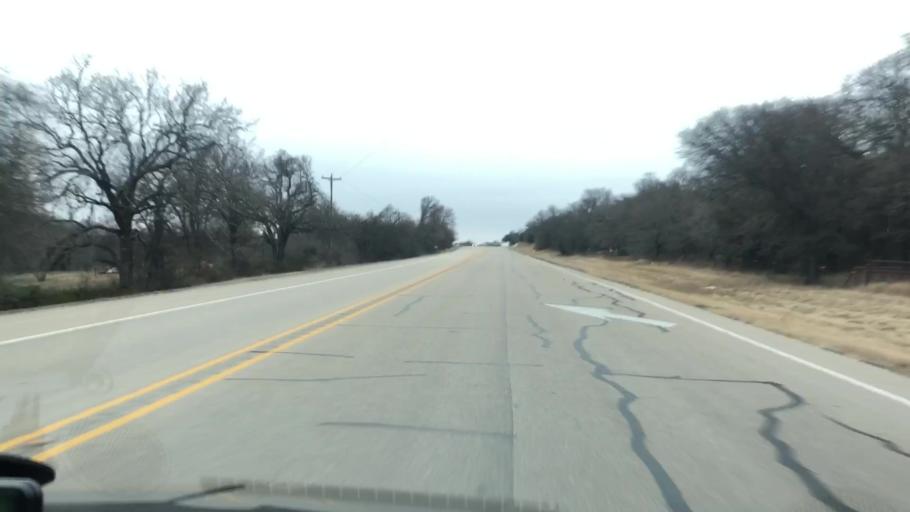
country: US
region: Texas
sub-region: Hamilton County
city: Hamilton
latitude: 31.7420
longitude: -98.1178
